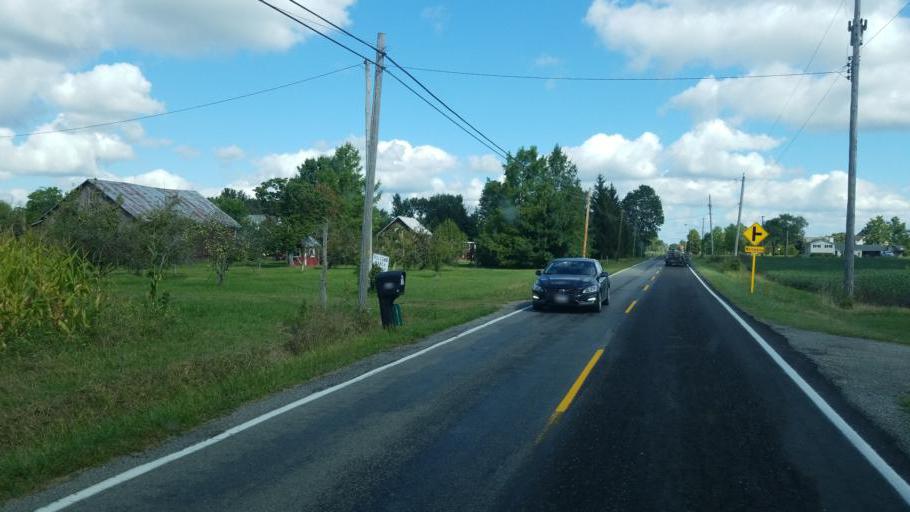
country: US
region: Ohio
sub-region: Lorain County
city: Lagrange
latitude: 41.2206
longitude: -82.1579
